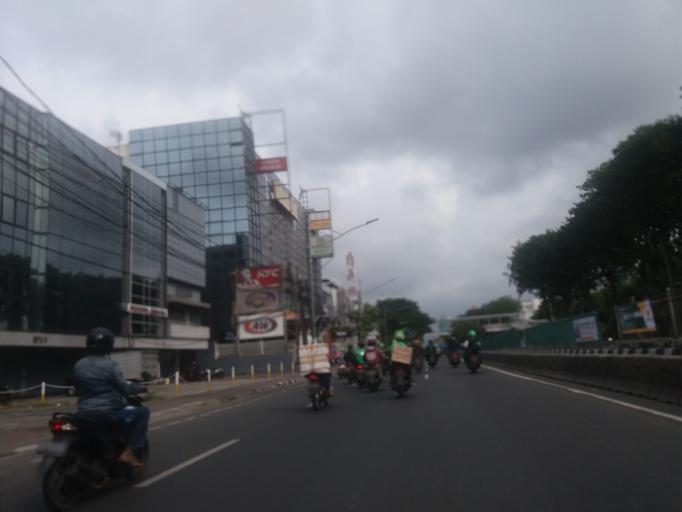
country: ID
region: Jakarta Raya
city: Jakarta
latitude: -6.1610
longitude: 106.8379
